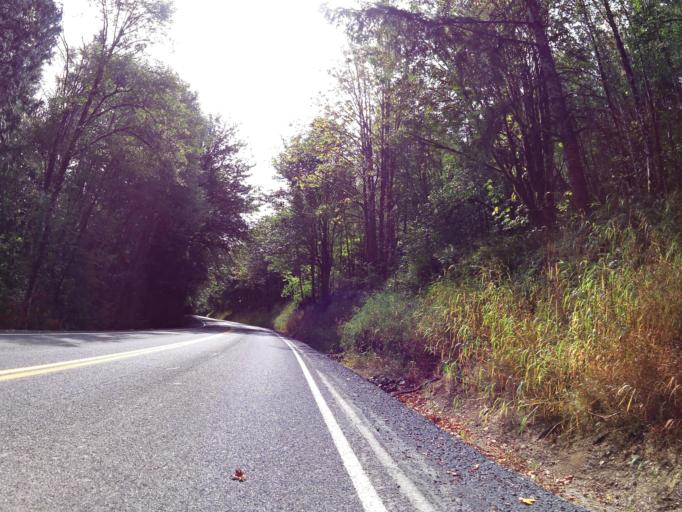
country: US
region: Washington
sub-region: Lewis County
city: Napavine
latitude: 46.5562
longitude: -122.9586
